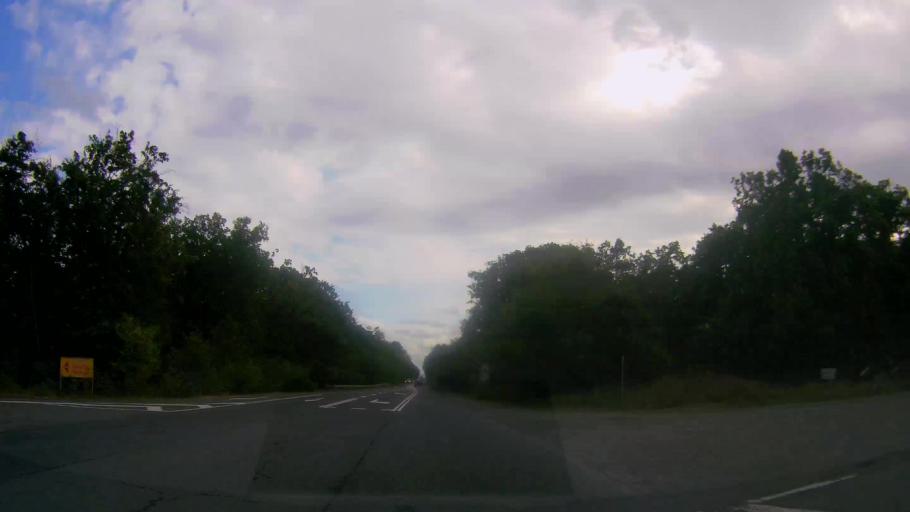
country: BG
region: Burgas
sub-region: Obshtina Primorsko
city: Primorsko
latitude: 42.2760
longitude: 27.7402
